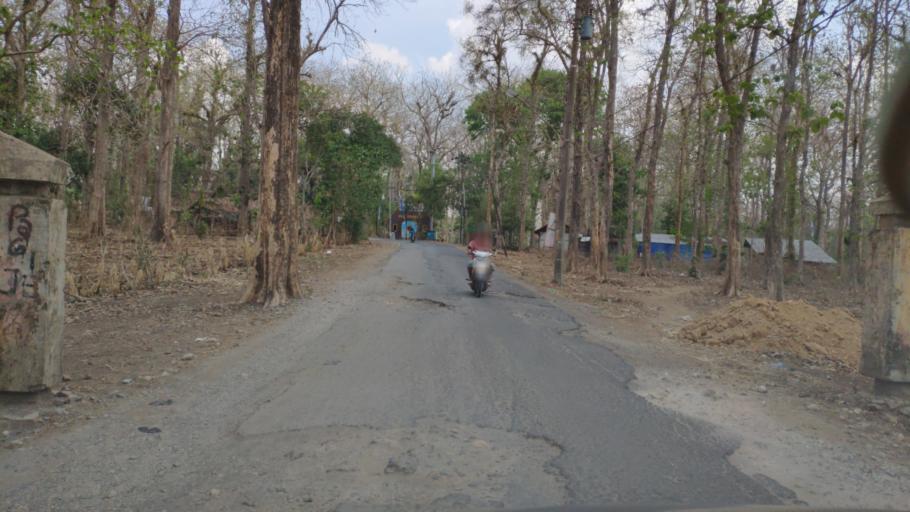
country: ID
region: Central Java
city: Ngapus
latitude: -6.9606
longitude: 111.1945
